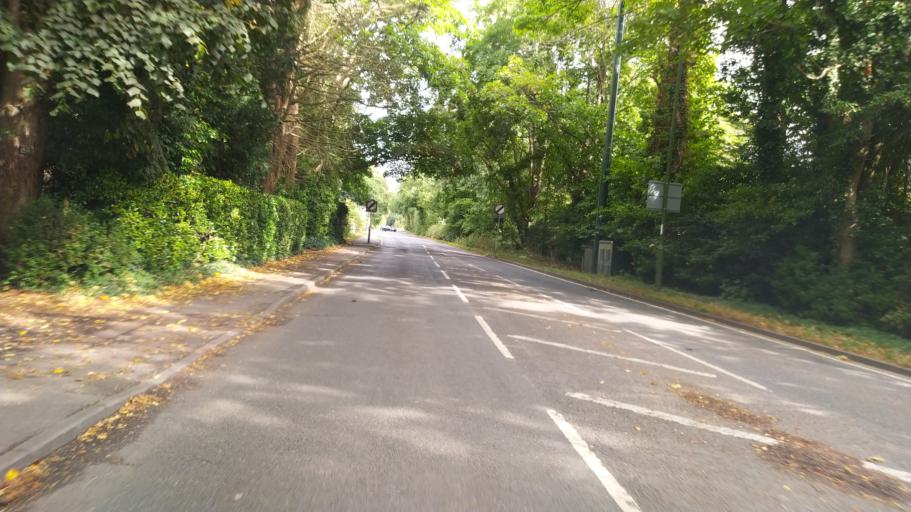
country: GB
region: England
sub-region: West Sussex
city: Chichester
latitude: 50.8579
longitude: -0.7832
